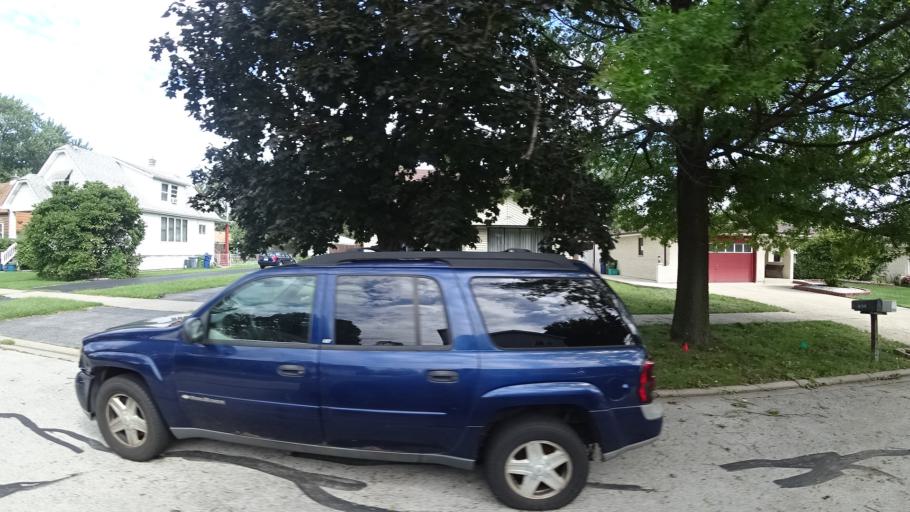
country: US
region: Illinois
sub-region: Cook County
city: Burbank
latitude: 41.7182
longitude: -87.7738
